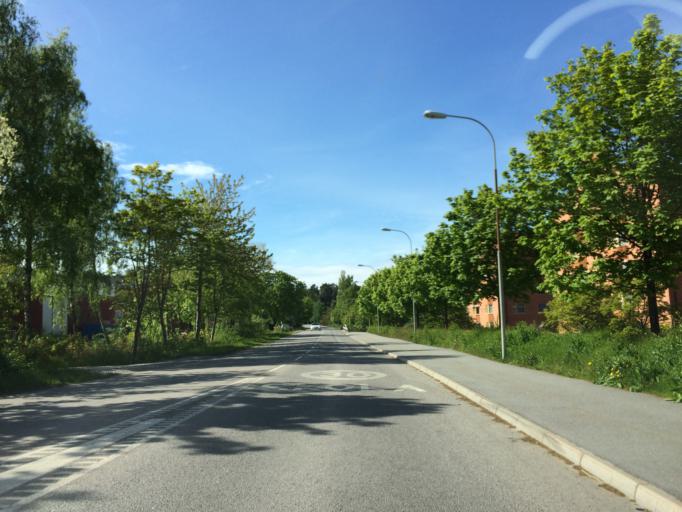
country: SE
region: Stockholm
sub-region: Sollentuna Kommun
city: Sollentuna
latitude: 59.4482
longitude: 17.9400
